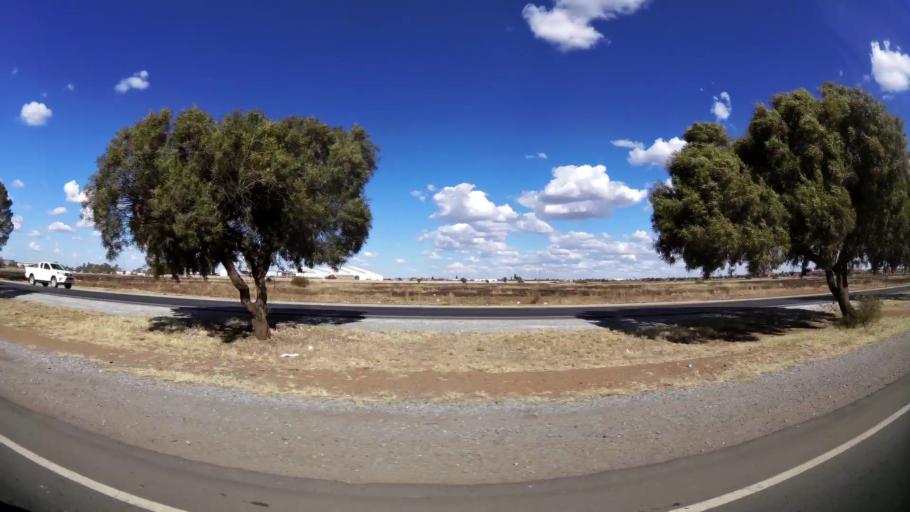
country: ZA
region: North-West
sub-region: Dr Kenneth Kaunda District Municipality
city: Klerksdorp
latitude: -26.8702
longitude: 26.6179
